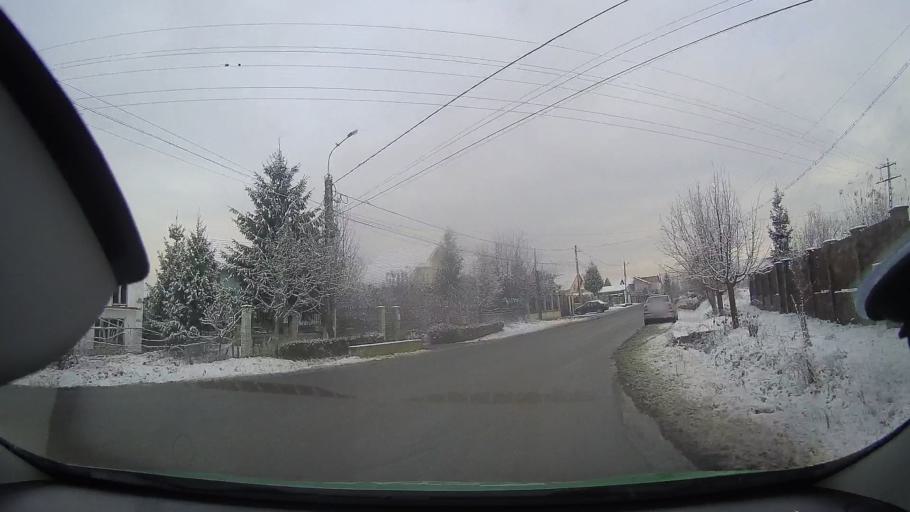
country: RO
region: Mures
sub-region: Comuna Bogata
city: Bogata
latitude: 46.4600
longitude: 24.0791
